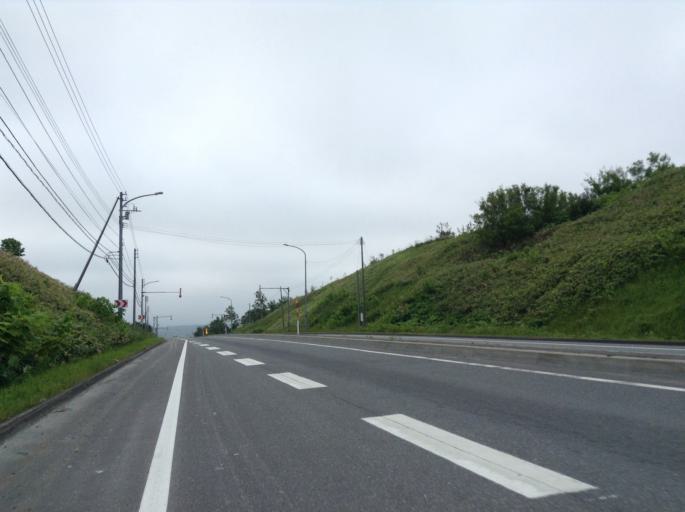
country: JP
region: Hokkaido
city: Wakkanai
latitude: 45.3739
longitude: 141.7162
